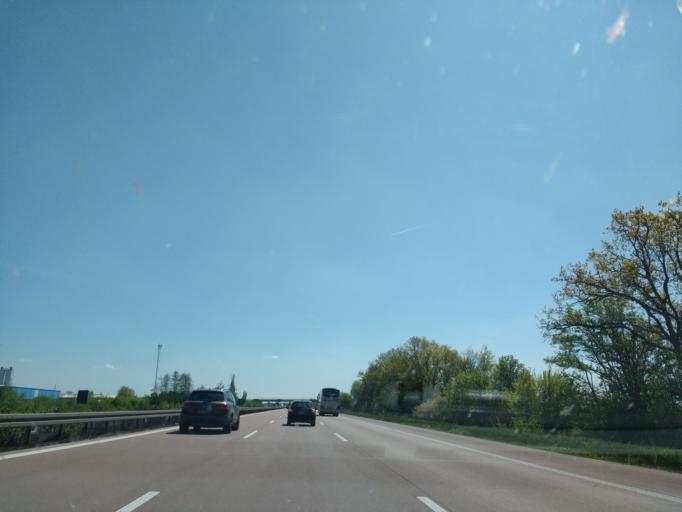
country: DE
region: Saxony-Anhalt
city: Dolbau
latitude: 51.4724
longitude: 12.0845
